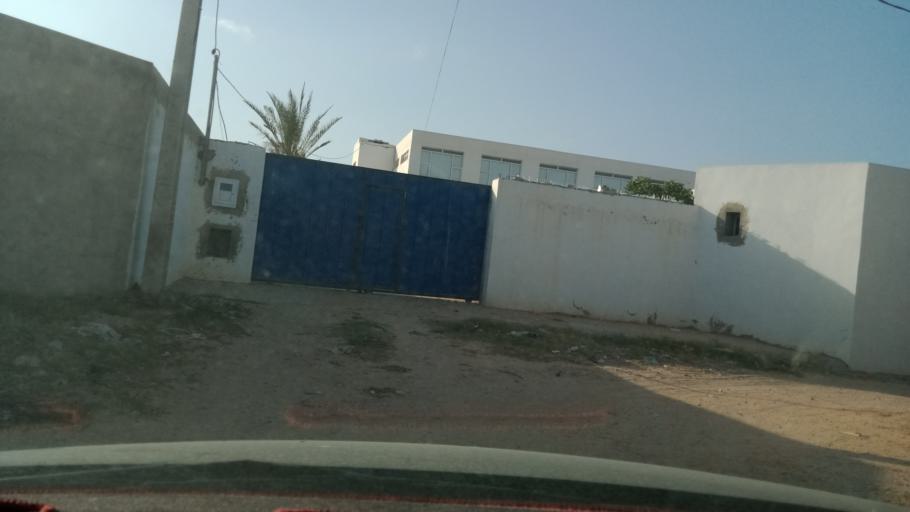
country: TN
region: Safaqis
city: Sfax
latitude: 34.8162
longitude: 10.7369
